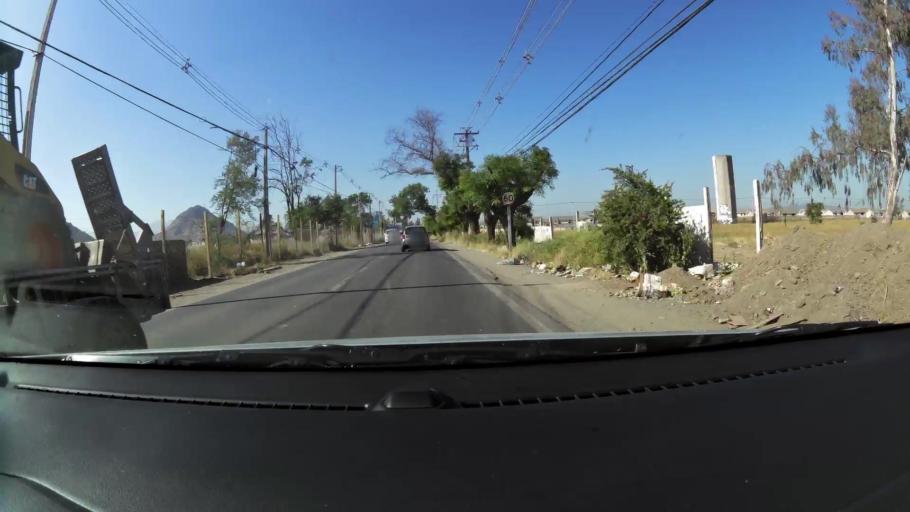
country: CL
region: Santiago Metropolitan
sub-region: Provincia de Maipo
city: San Bernardo
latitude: -33.6063
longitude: -70.6829
